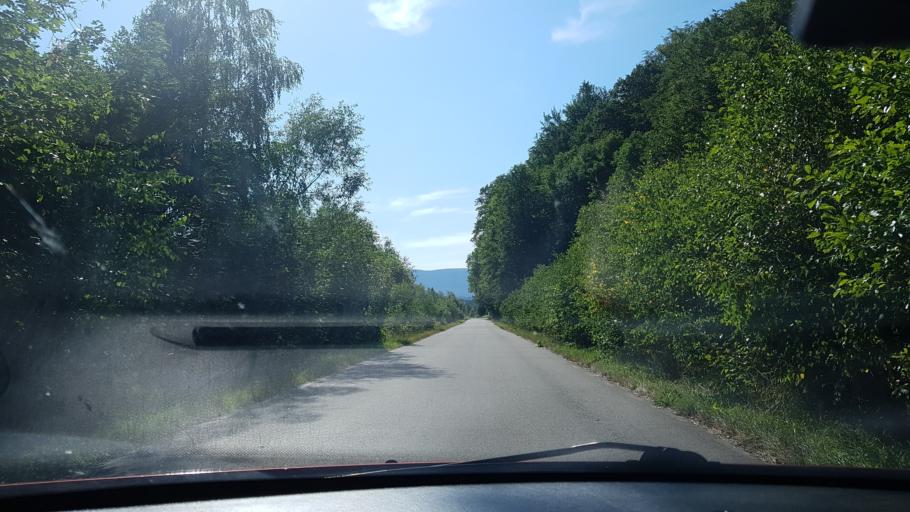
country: PL
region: Lower Silesian Voivodeship
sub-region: Powiat klodzki
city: Miedzylesie
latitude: 50.2332
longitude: 16.7325
